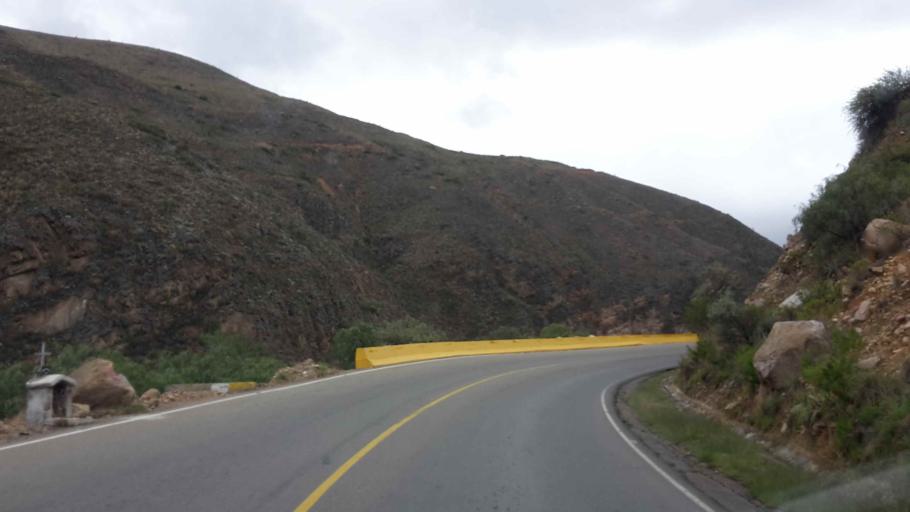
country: BO
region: Cochabamba
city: Punata
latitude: -17.5046
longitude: -65.7982
